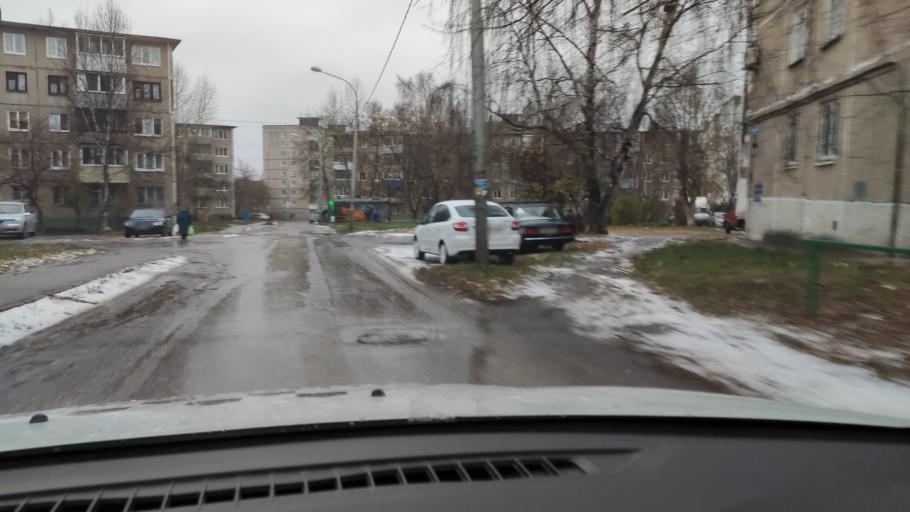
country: RU
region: Perm
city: Kondratovo
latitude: 57.9671
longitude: 56.1659
